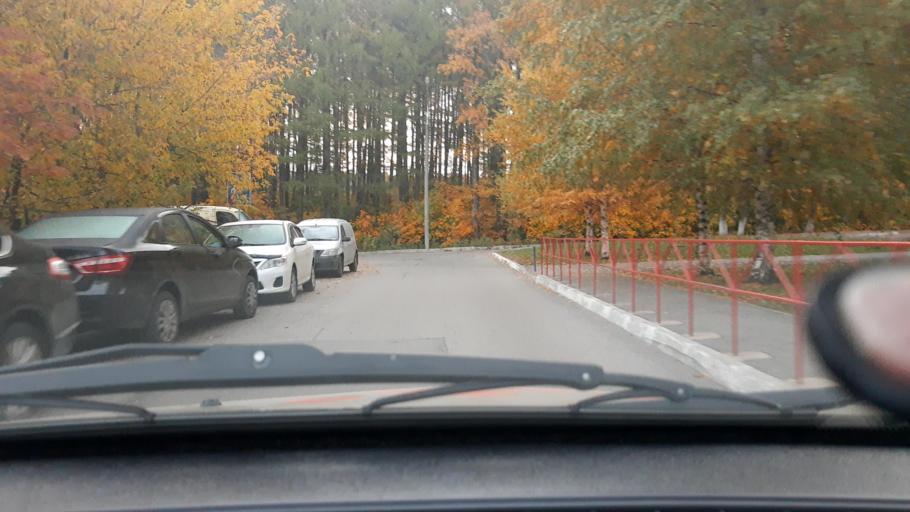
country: RU
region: Bashkortostan
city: Ufa
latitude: 54.7188
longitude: 56.0143
